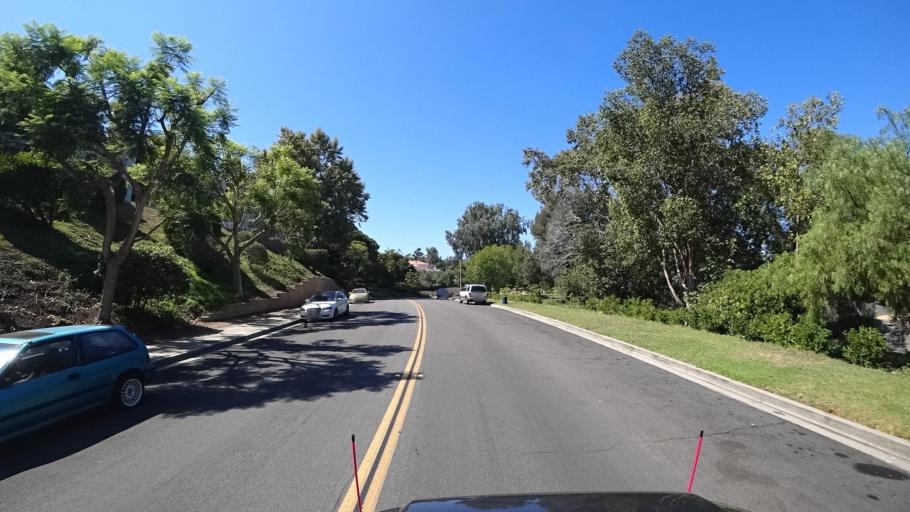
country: US
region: California
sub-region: San Diego County
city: Lake San Marcos
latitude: 33.1209
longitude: -117.2116
